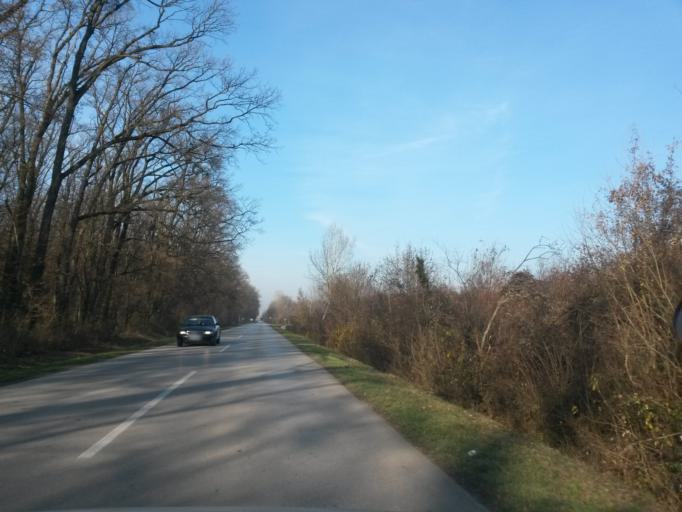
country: HR
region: Vukovarsko-Srijemska
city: Privlaka
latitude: 45.2172
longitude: 18.8571
